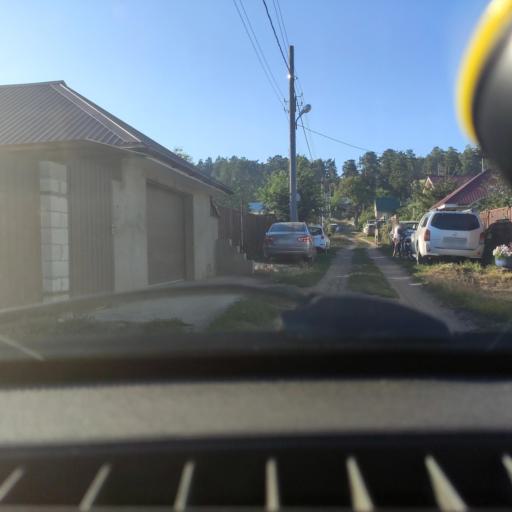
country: RU
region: Samara
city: Zhigulevsk
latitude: 53.4699
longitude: 49.5916
